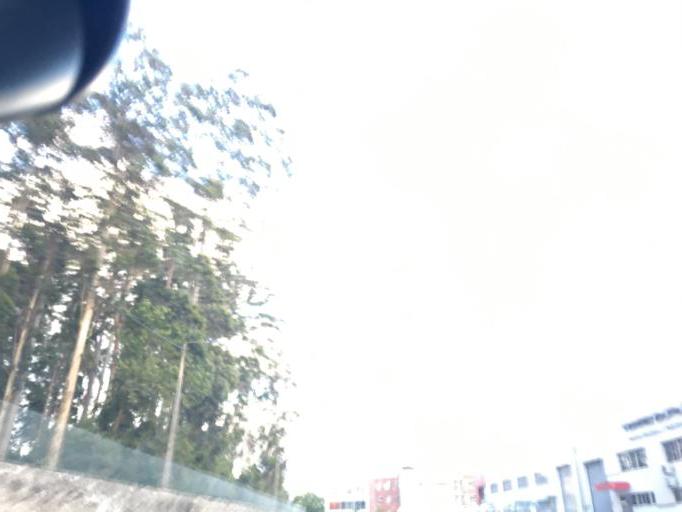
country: PT
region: Porto
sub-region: Maia
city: Anta
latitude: 41.2750
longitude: -8.6100
